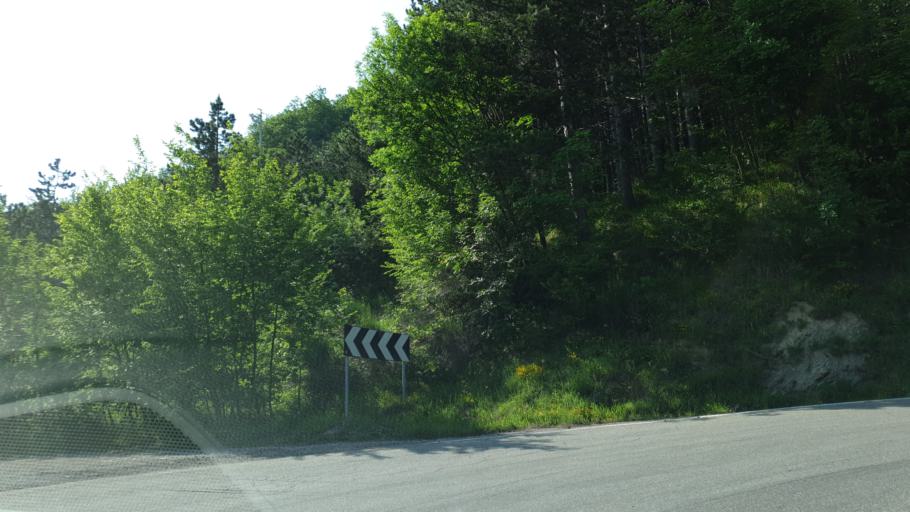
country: IT
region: Emilia-Romagna
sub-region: Forli-Cesena
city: San Piero in Bagno
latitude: 43.8150
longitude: 11.9473
